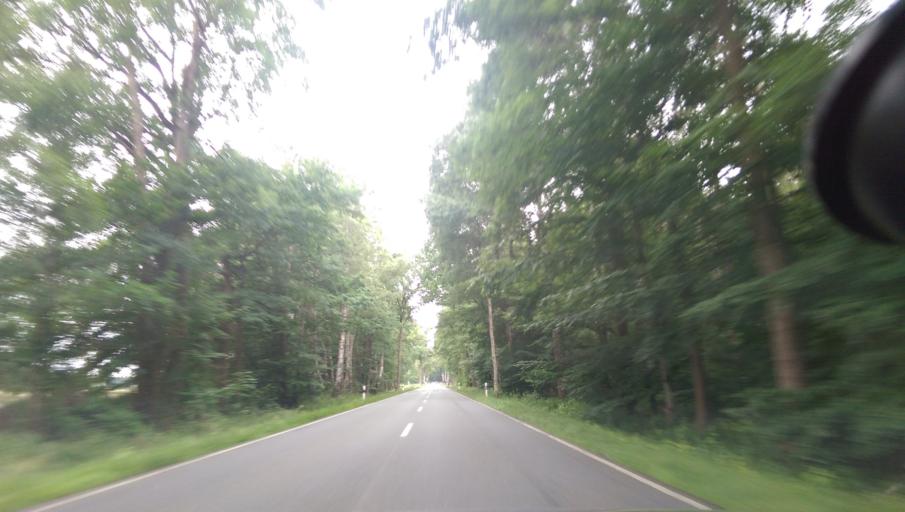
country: DE
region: Lower Saxony
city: Bomlitz
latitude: 52.9449
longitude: 9.6777
